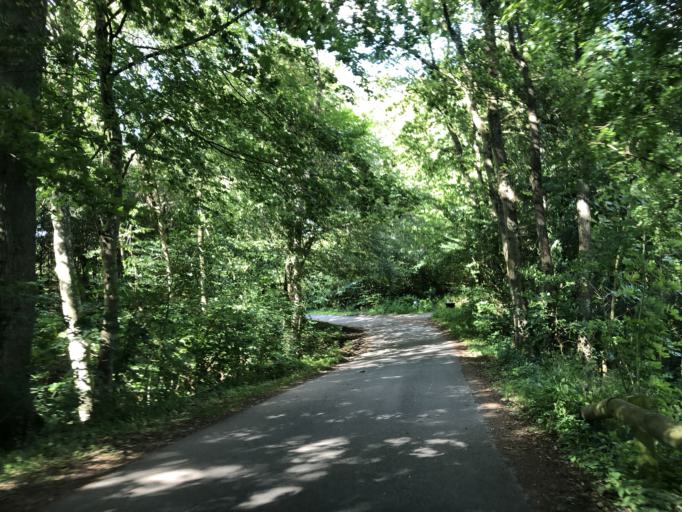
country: DK
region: South Denmark
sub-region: Vejle Kommune
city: Brejning
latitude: 55.6799
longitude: 9.6625
